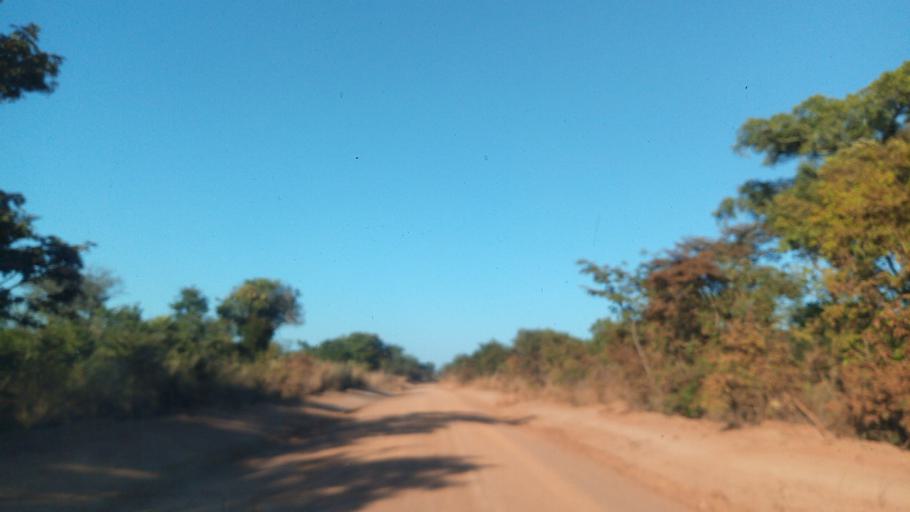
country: ZM
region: Luapula
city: Mwense
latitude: -10.4729
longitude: 28.5151
